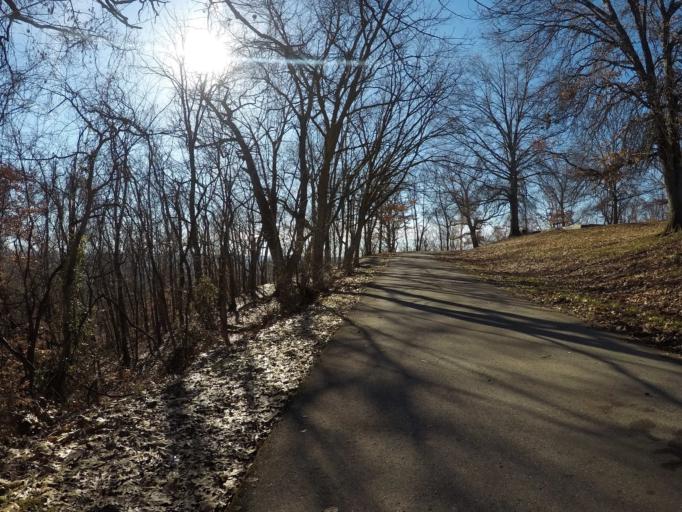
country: US
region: West Virginia
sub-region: Cabell County
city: Huntington
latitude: 38.4178
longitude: -82.3957
